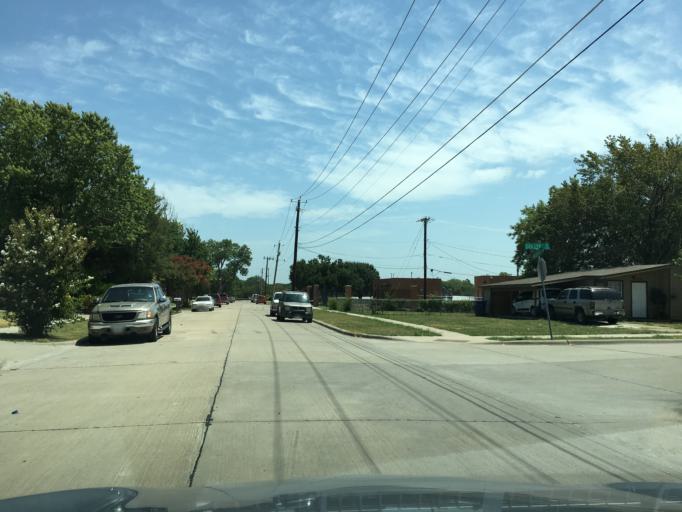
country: US
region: Texas
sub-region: Dallas County
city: Garland
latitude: 32.8924
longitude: -96.6250
